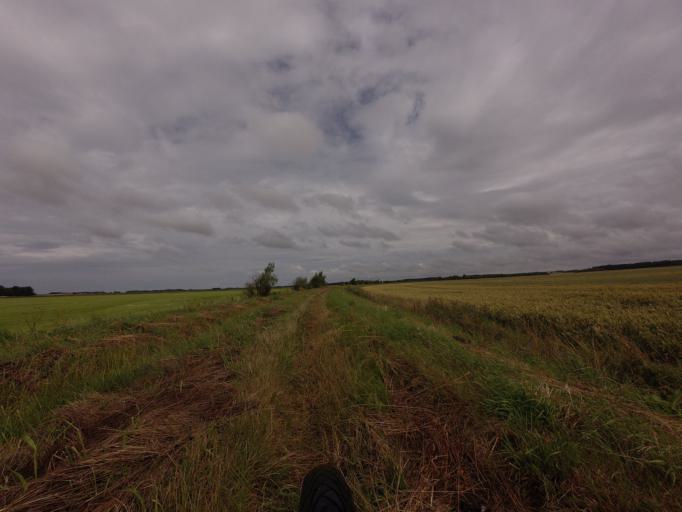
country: DK
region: North Denmark
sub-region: Jammerbugt Kommune
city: Pandrup
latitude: 57.3158
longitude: 9.7440
